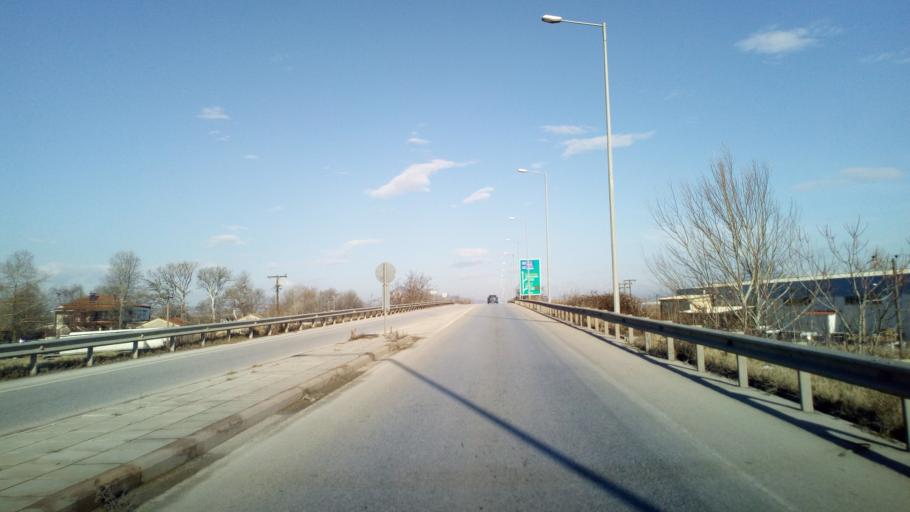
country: GR
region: Central Macedonia
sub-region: Nomos Thessalonikis
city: Lagyna
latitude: 40.7300
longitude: 23.0137
